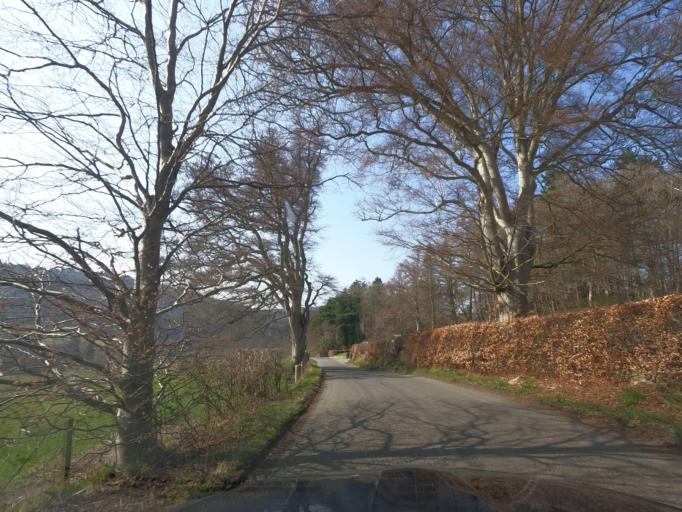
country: GB
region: Scotland
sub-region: The Scottish Borders
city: Selkirk
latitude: 55.5858
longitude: -2.8477
